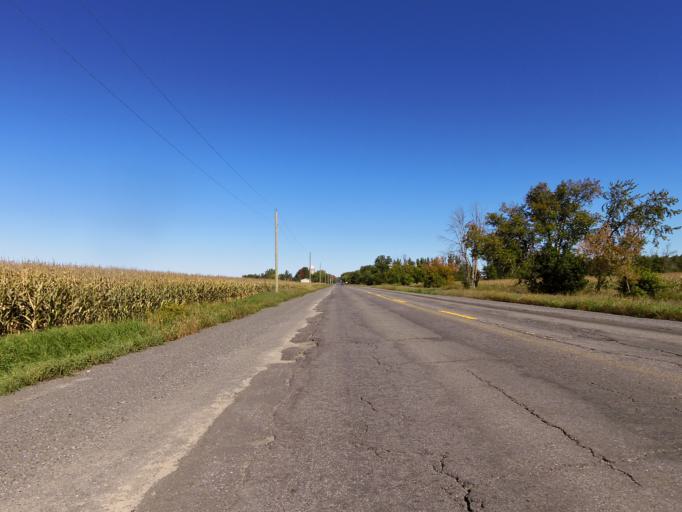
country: CA
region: Ontario
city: Clarence-Rockland
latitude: 45.3953
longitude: -75.4323
